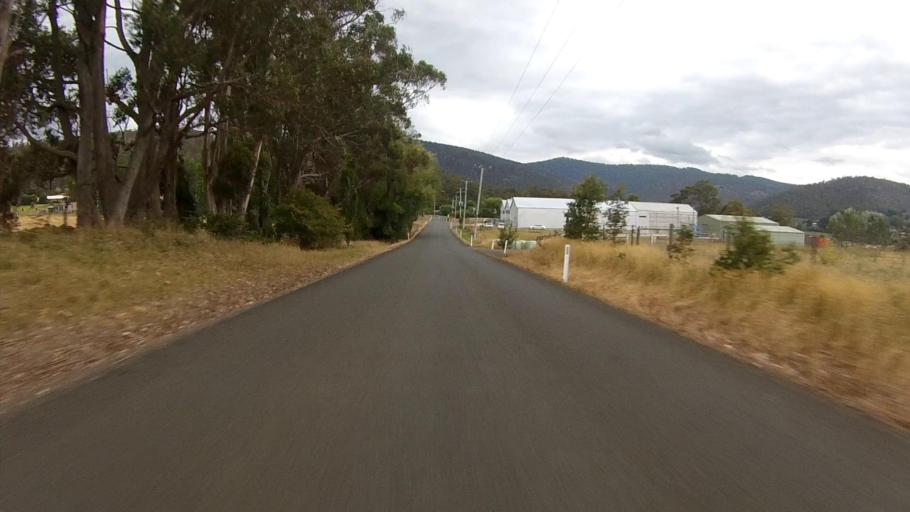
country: AU
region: Tasmania
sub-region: Huon Valley
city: Huonville
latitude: -42.9776
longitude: 147.0956
